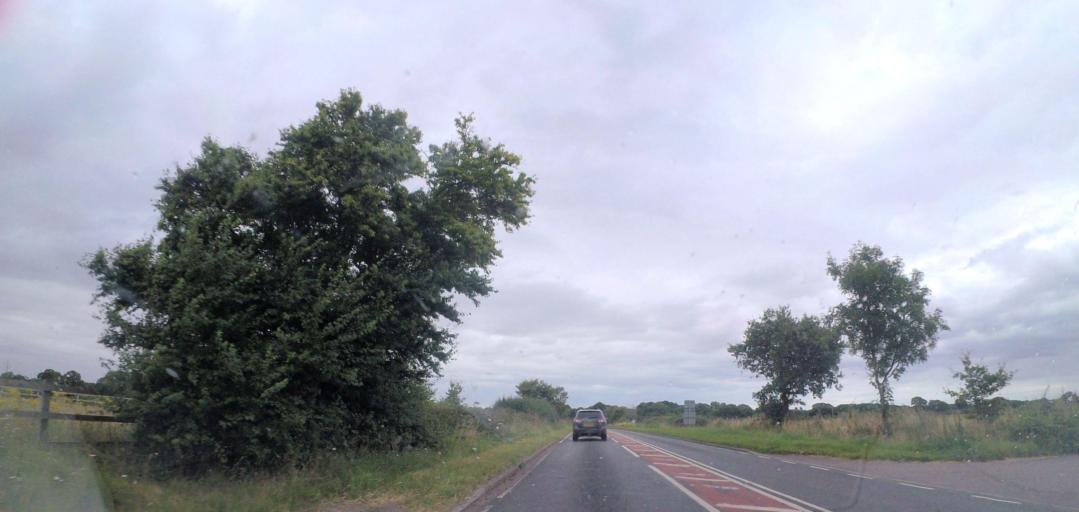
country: GB
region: England
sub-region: Norfolk
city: Spixworth
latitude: 52.6890
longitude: 1.3347
